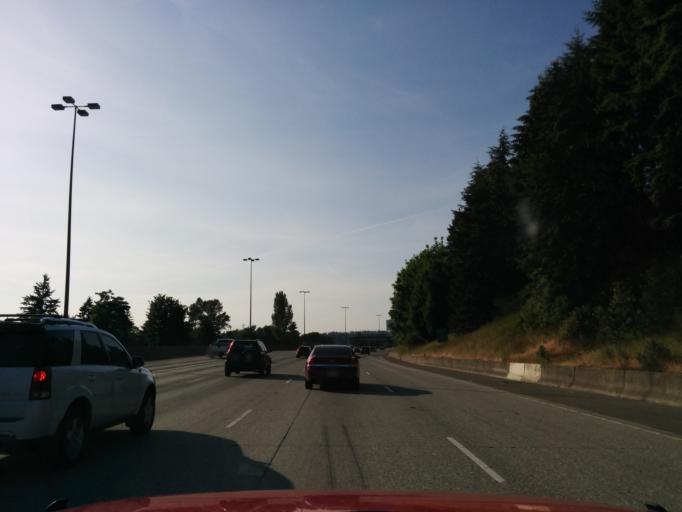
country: US
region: Washington
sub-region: King County
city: Newport
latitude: 47.5852
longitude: -122.1777
